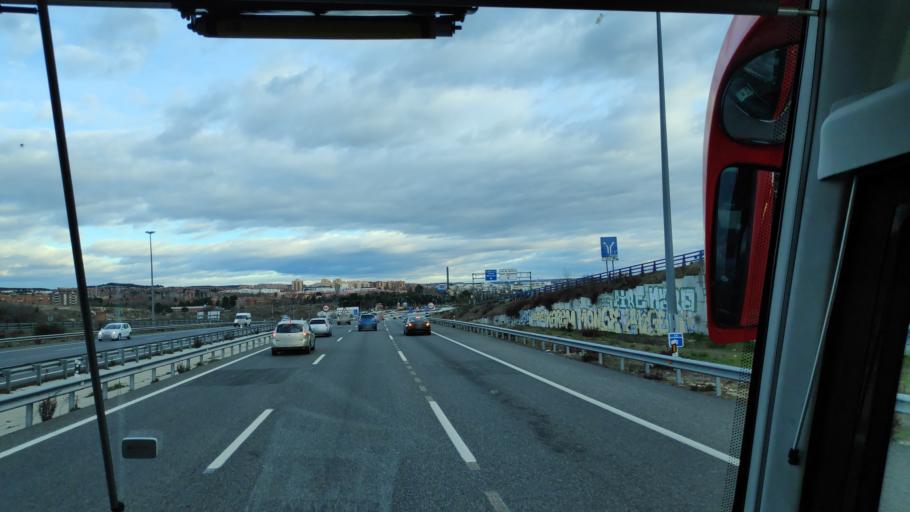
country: ES
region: Madrid
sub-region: Provincia de Madrid
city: Villa de Vallecas
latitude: 40.3590
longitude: -3.5611
